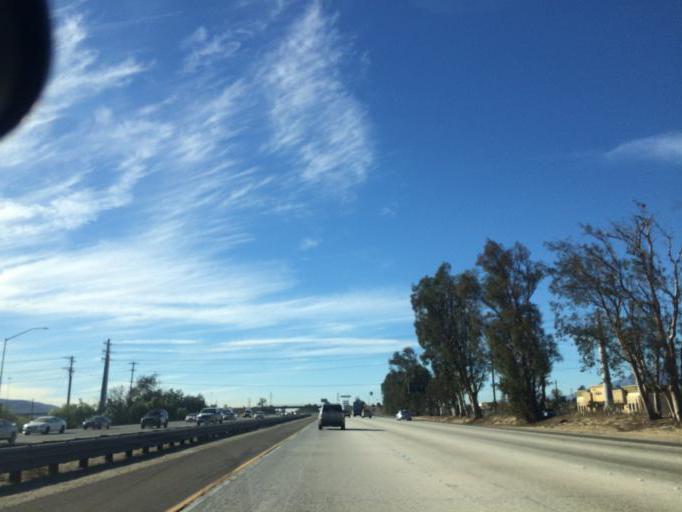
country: US
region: California
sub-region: San Bernardino County
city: Colton
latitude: 34.0688
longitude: -117.3467
